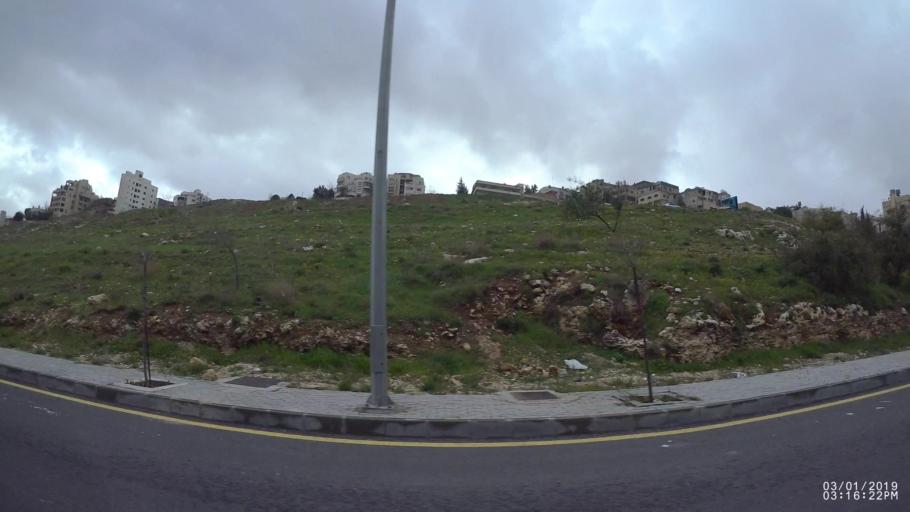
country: JO
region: Amman
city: Amman
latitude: 31.9489
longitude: 35.9029
